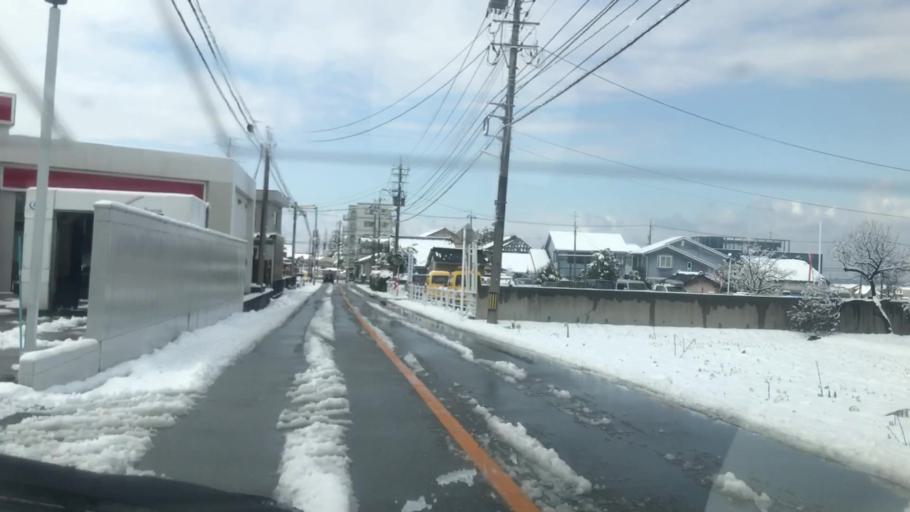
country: JP
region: Toyama
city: Toyama-shi
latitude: 36.6306
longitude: 137.2323
